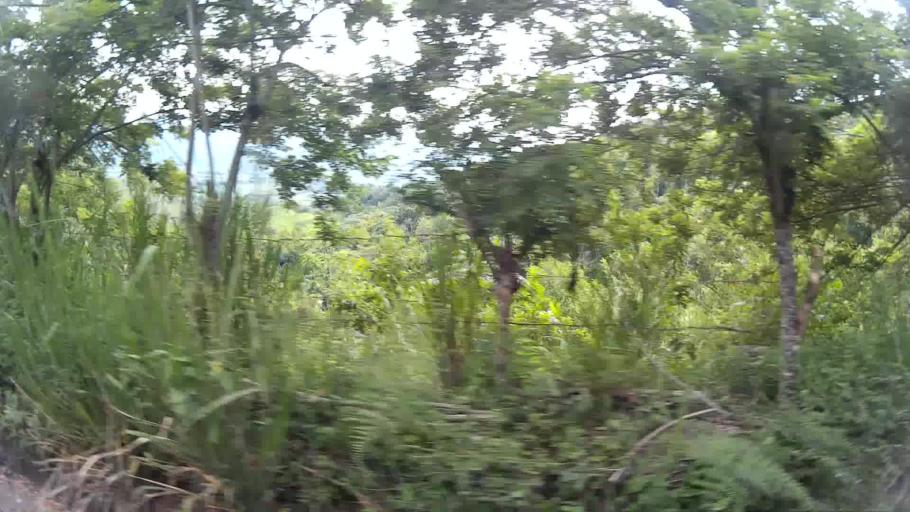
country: CO
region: Risaralda
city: La Virginia
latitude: 4.9404
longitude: -75.8432
